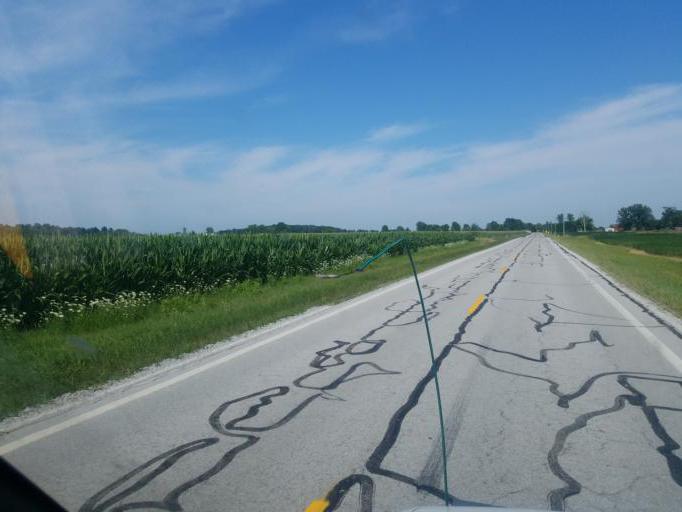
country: US
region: Ohio
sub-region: Logan County
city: Lakeview
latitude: 40.6012
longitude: -83.8916
